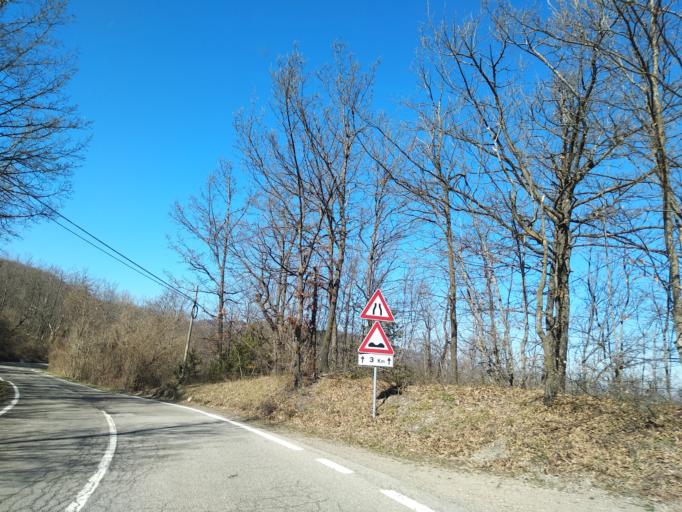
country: IT
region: Emilia-Romagna
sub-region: Provincia di Reggio Emilia
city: Ramiseto
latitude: 44.4081
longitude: 10.3115
